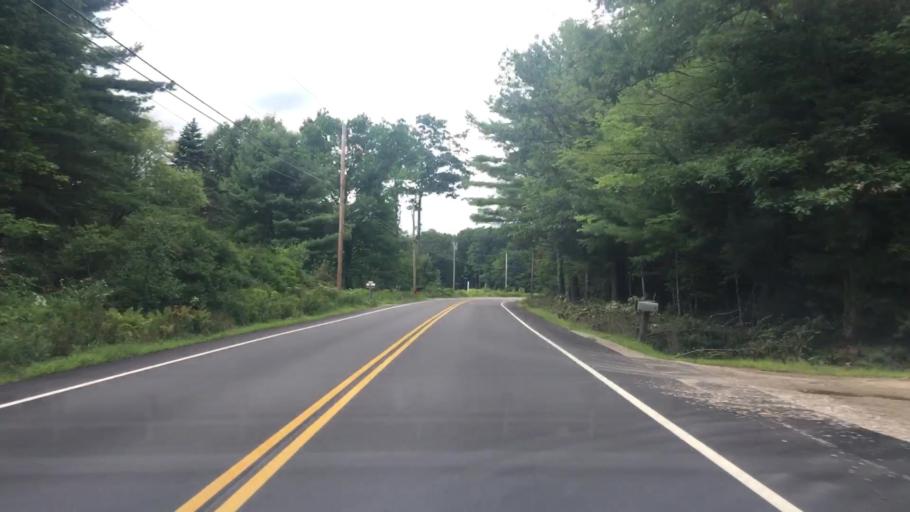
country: US
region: Maine
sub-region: York County
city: West Kennebunk
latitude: 43.4741
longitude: -70.6022
